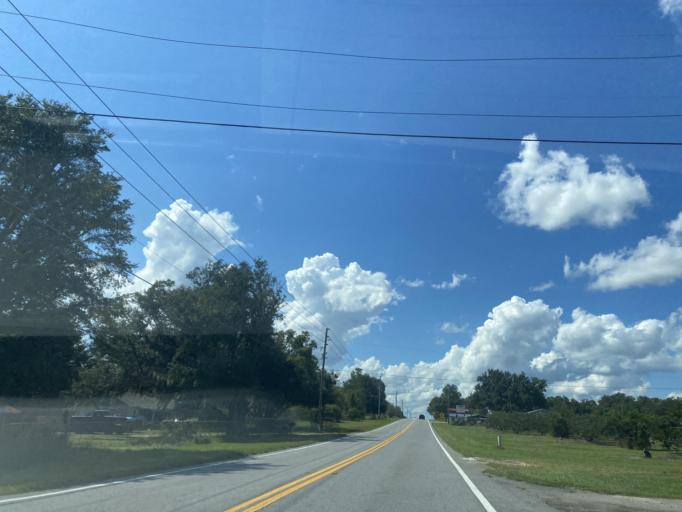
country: US
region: Florida
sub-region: Lake County
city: Lady Lake
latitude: 28.9802
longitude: -81.8761
